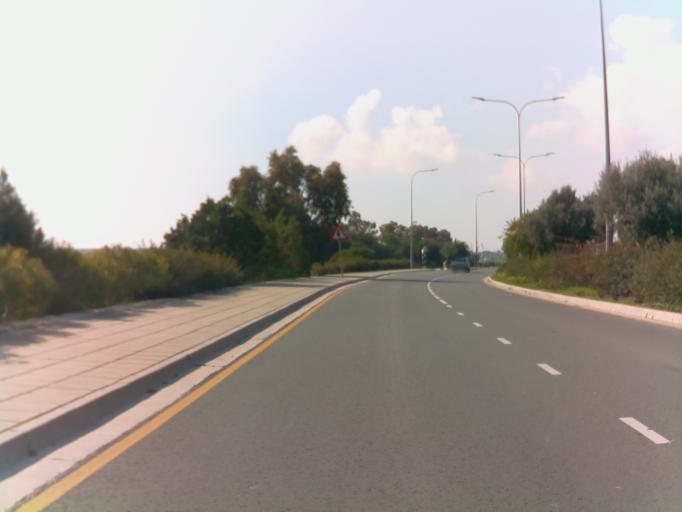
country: CY
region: Larnaka
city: Meneou
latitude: 34.8786
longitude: 33.6166
